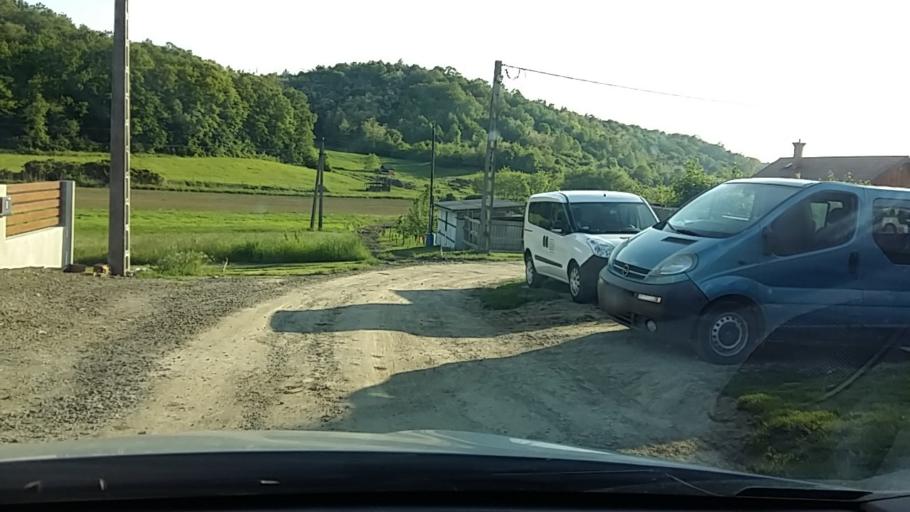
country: HU
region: Pest
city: Kosd
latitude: 47.7961
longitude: 19.2495
